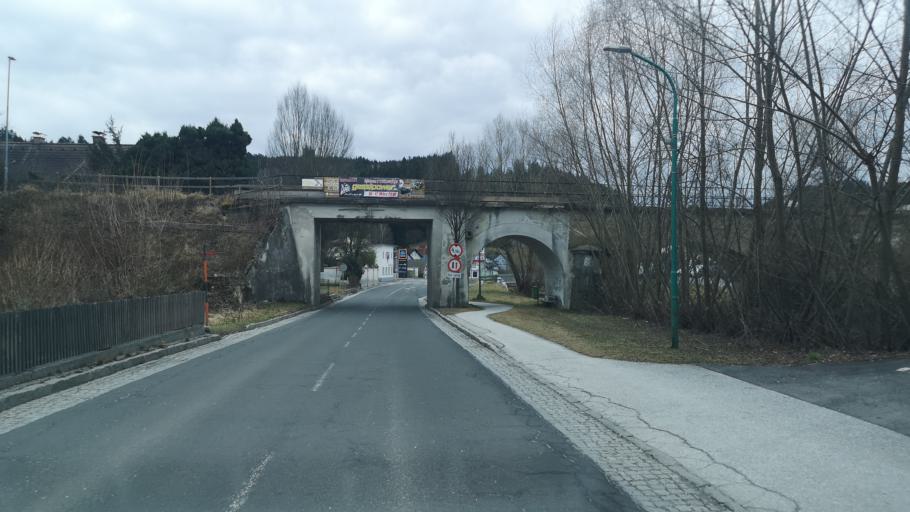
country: AT
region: Styria
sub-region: Politischer Bezirk Weiz
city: Birkfeld
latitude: 47.3558
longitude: 15.6999
